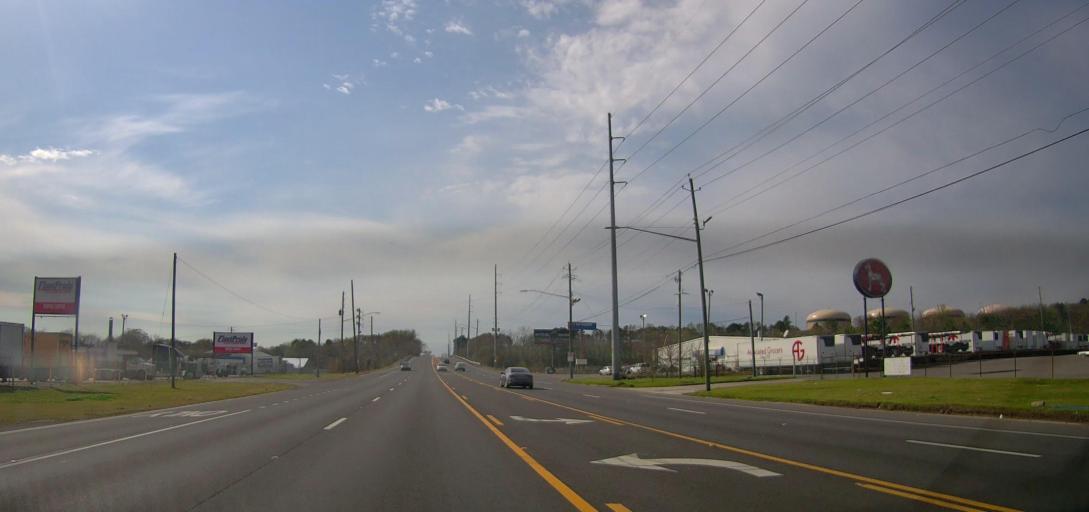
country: US
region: Alabama
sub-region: Jefferson County
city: Forestdale
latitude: 33.5329
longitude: -86.8576
